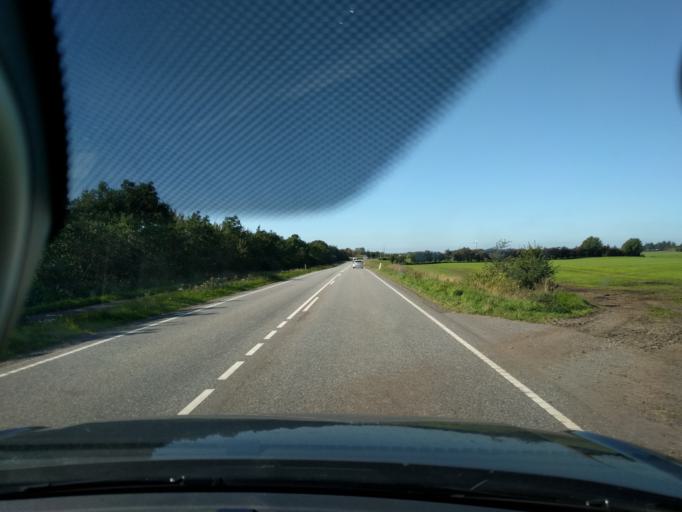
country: DK
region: North Denmark
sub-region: Mariagerfjord Kommune
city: Hobro
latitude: 56.6776
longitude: 9.6690
